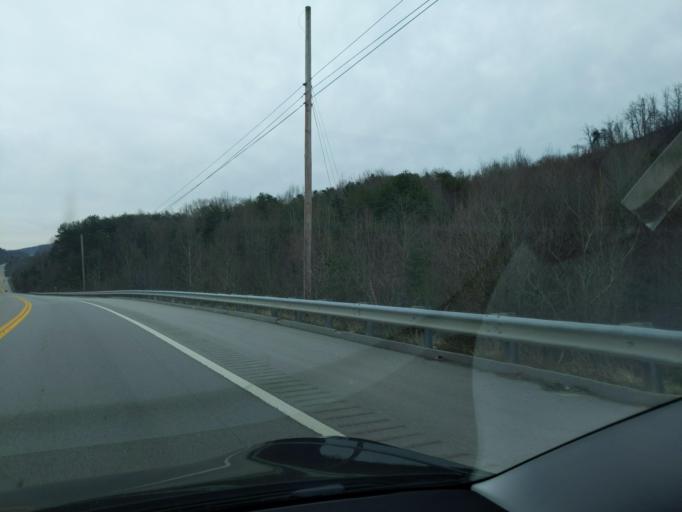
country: US
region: Kentucky
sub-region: Whitley County
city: Corbin
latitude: 36.9176
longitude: -84.1000
